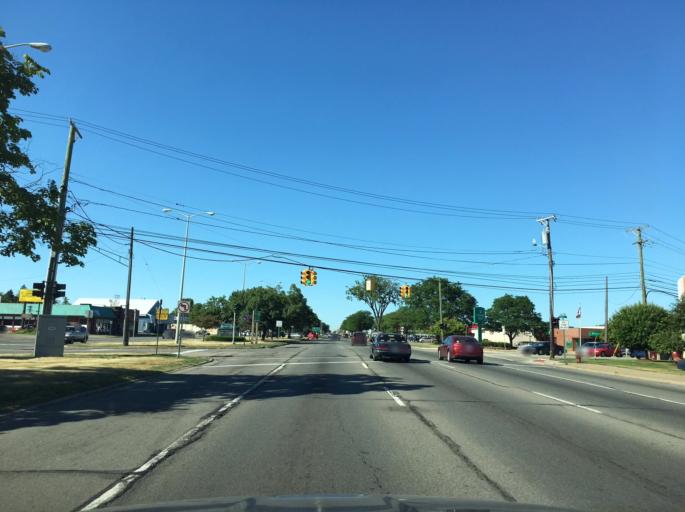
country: US
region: Michigan
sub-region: Macomb County
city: Roseville
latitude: 42.4868
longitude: -82.9432
